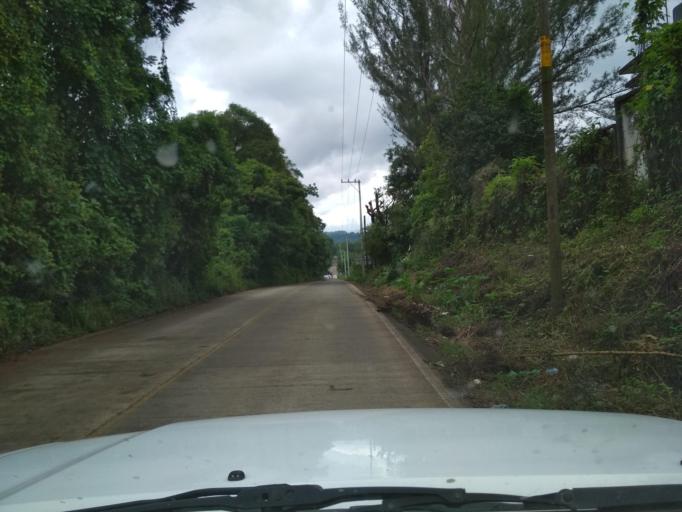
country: MX
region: Veracruz
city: Comoapan
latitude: 18.4202
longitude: -95.1772
